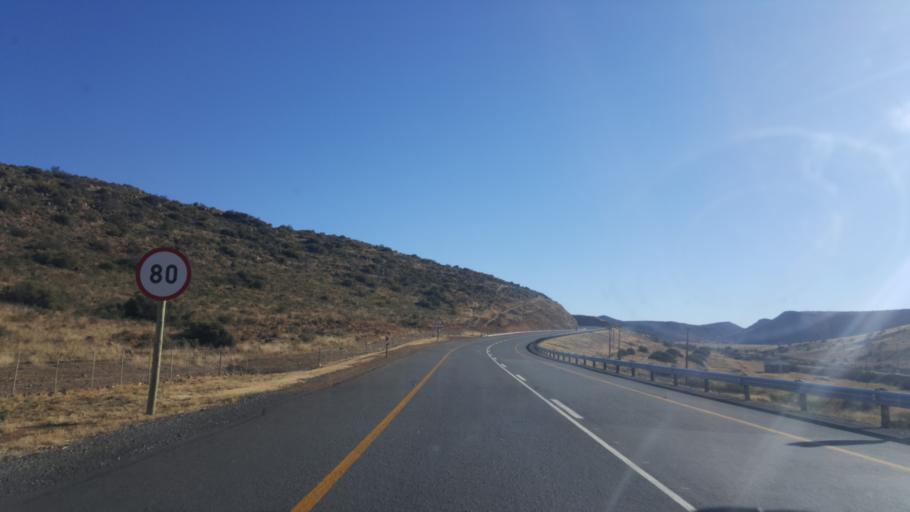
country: ZA
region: Eastern Cape
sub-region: Chris Hani District Municipality
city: Middelburg
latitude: -31.3839
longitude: 25.0321
